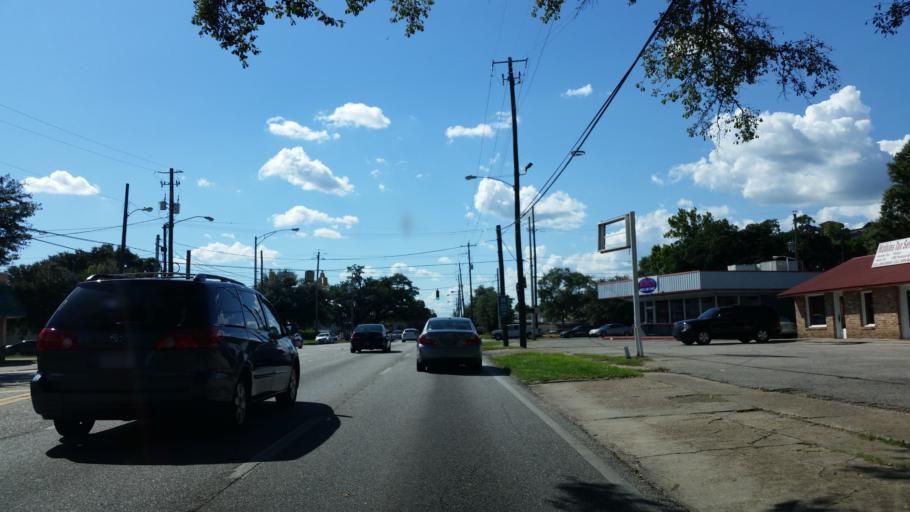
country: US
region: Alabama
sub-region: Mobile County
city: Prichard
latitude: 30.6966
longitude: -88.1029
